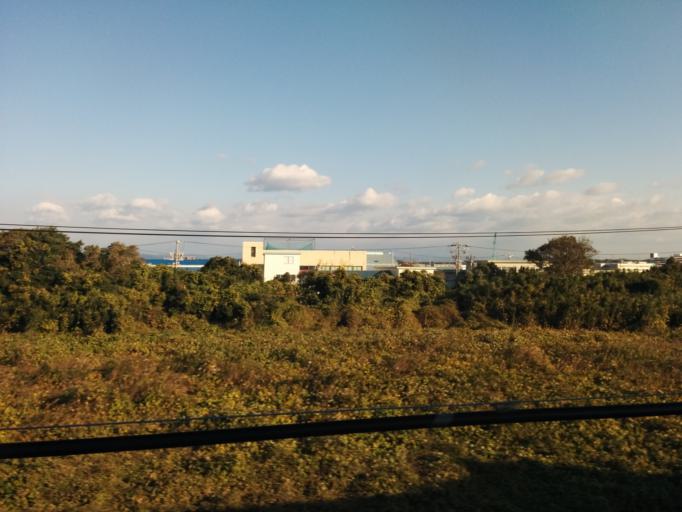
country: JP
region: Shizuoka
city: Hamamatsu
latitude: 34.6874
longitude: 137.6403
